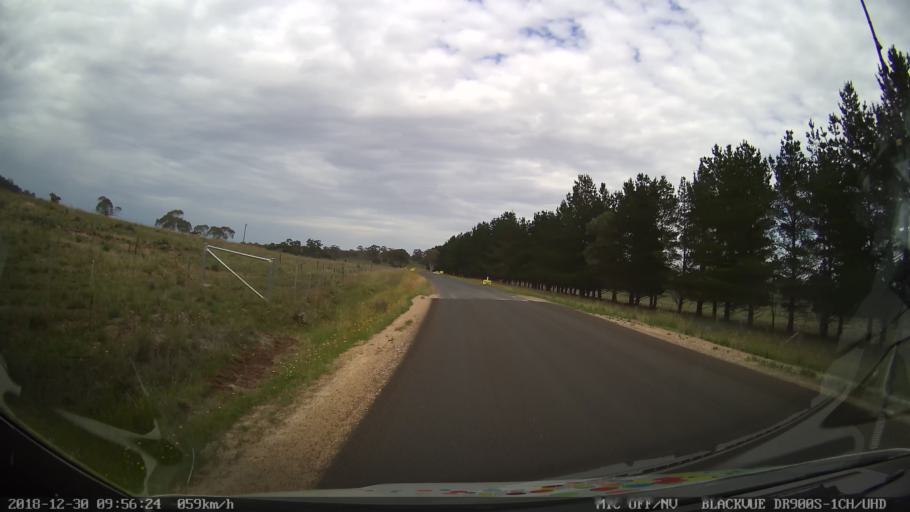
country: AU
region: New South Wales
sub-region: Cooma-Monaro
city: Cooma
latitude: -36.5223
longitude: 149.2521
